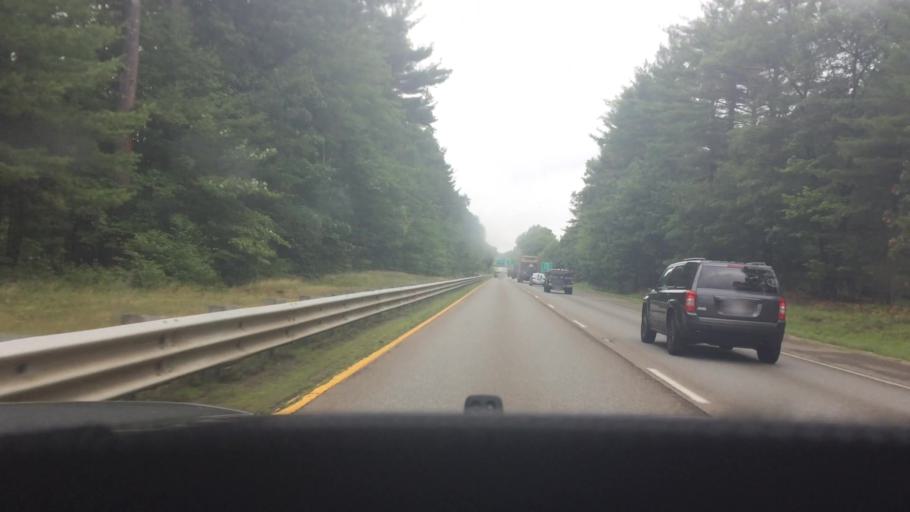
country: US
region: Massachusetts
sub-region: Middlesex County
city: Shirley
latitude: 42.5187
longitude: -71.6841
